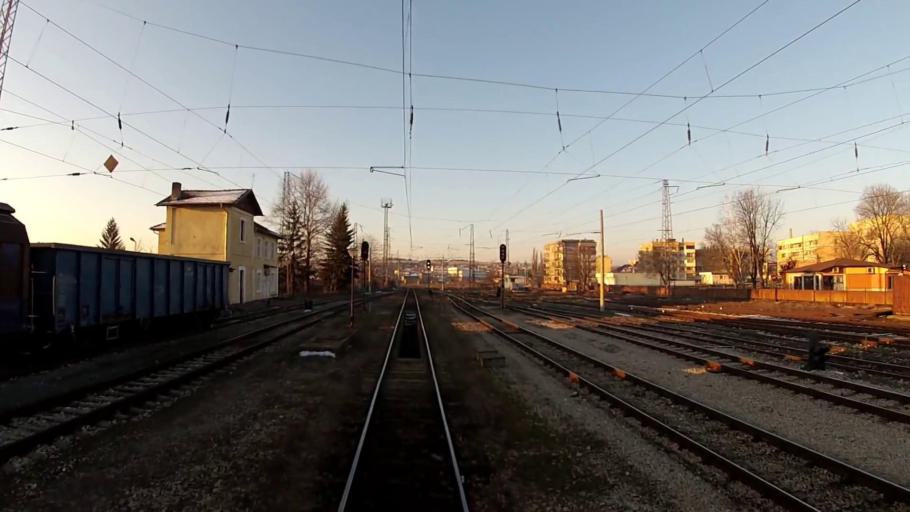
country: BG
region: Sofiya
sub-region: Obshtina Dragoman
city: Dragoman
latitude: 42.9189
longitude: 22.9297
